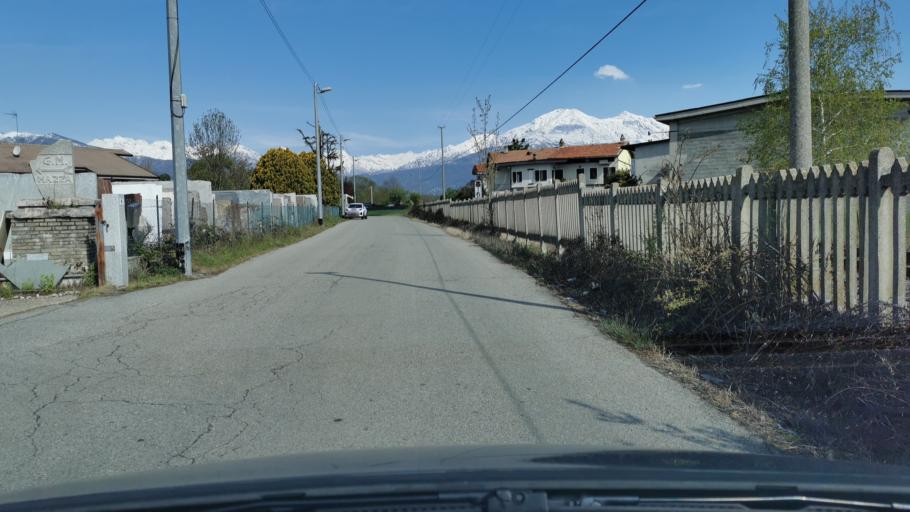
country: IT
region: Piedmont
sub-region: Provincia di Torino
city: Oglianico
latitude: 45.3395
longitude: 7.6878
